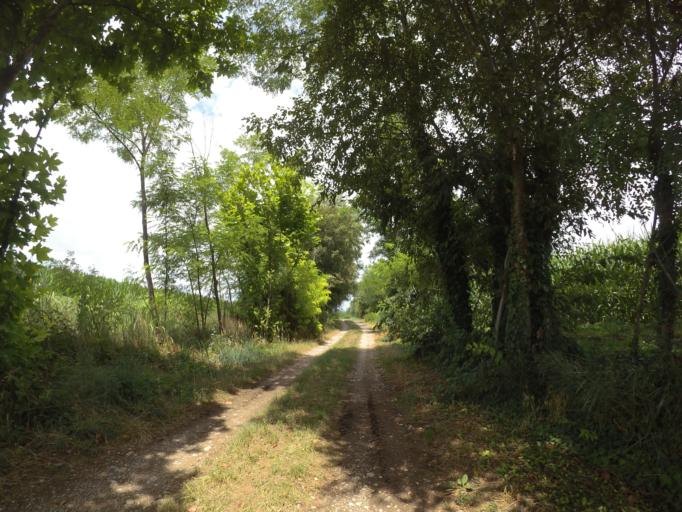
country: IT
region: Friuli Venezia Giulia
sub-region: Provincia di Udine
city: Bertiolo
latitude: 45.9636
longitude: 13.0646
